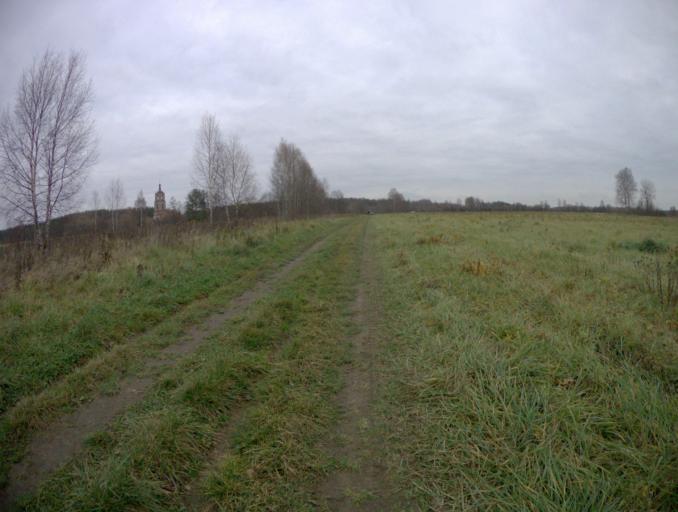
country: RU
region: Moskovskaya
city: Malaya Dubna
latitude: 55.9910
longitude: 38.9912
